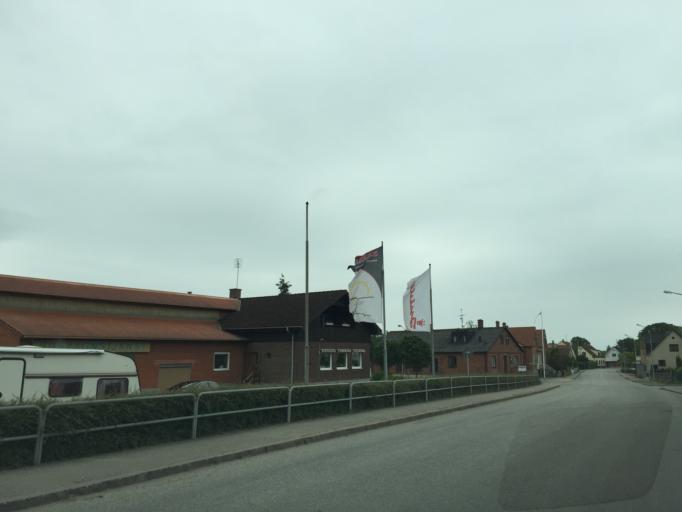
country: SE
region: Skane
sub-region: Ystads Kommun
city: Kopingebro
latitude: 55.4391
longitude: 14.1125
